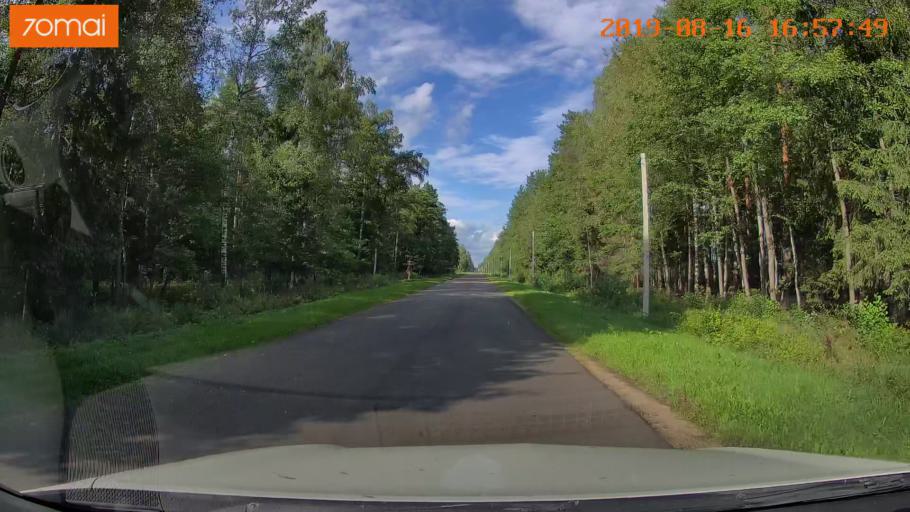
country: BY
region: Mogilev
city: Hlusha
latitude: 53.2612
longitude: 28.8279
